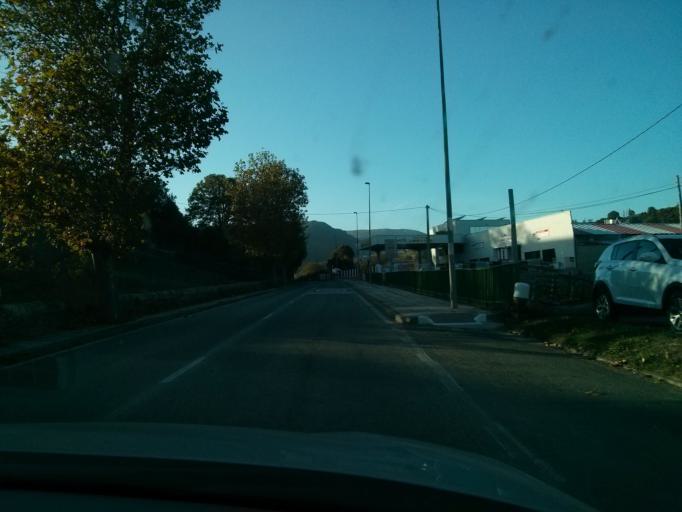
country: ES
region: Castille and Leon
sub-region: Provincia de Burgos
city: Espinosa de los Monteros
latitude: 43.0747
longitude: -3.5413
